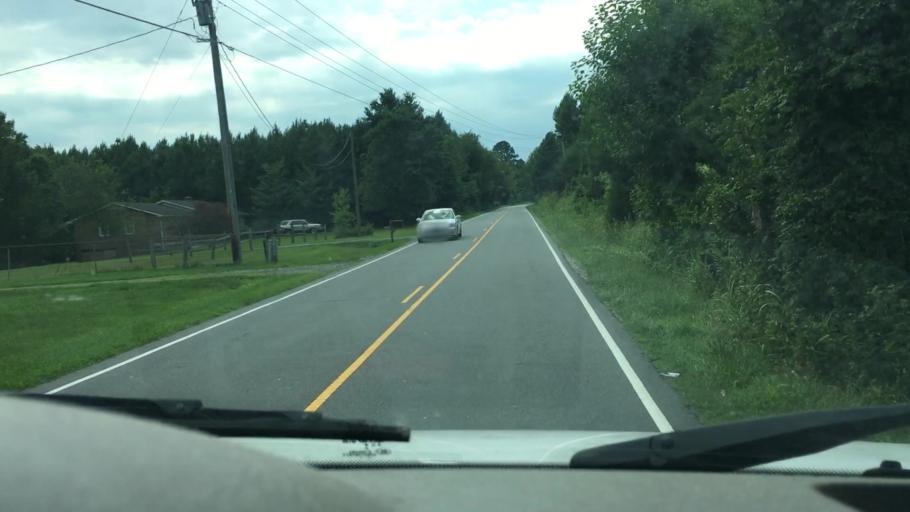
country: US
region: North Carolina
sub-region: Gaston County
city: Davidson
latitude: 35.4834
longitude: -80.8156
